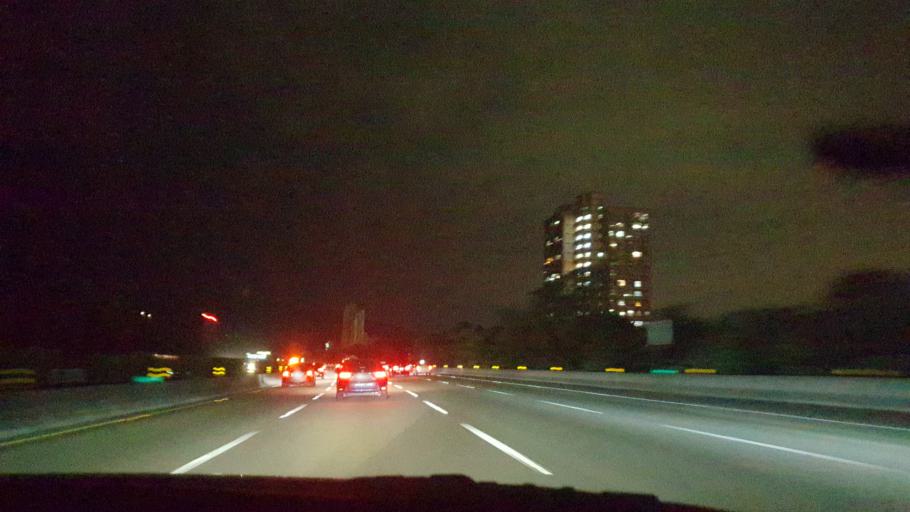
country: TW
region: Taipei
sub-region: Taipei
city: Banqiao
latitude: 24.9723
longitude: 121.4458
